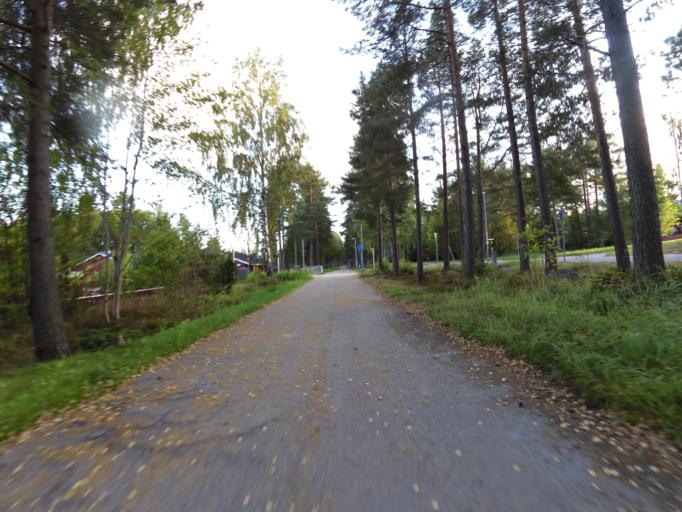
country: SE
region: Gaevleborg
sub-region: Gavle Kommun
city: Gavle
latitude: 60.6732
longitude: 17.2295
